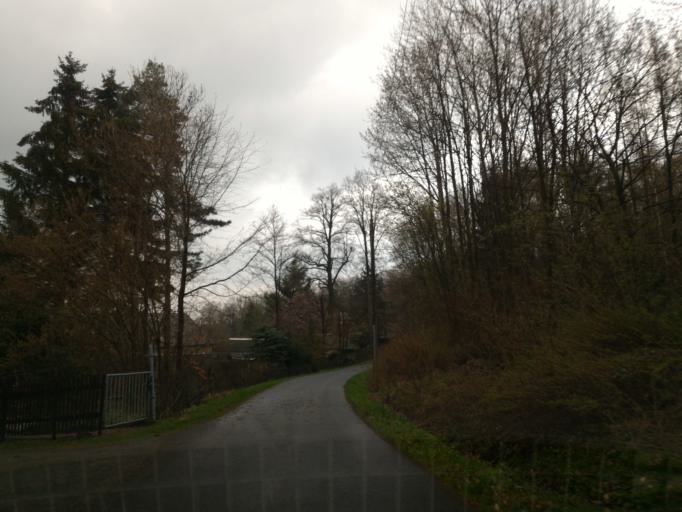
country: DE
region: Saxony
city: Kurort Jonsdorf
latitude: 50.8598
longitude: 14.7236
